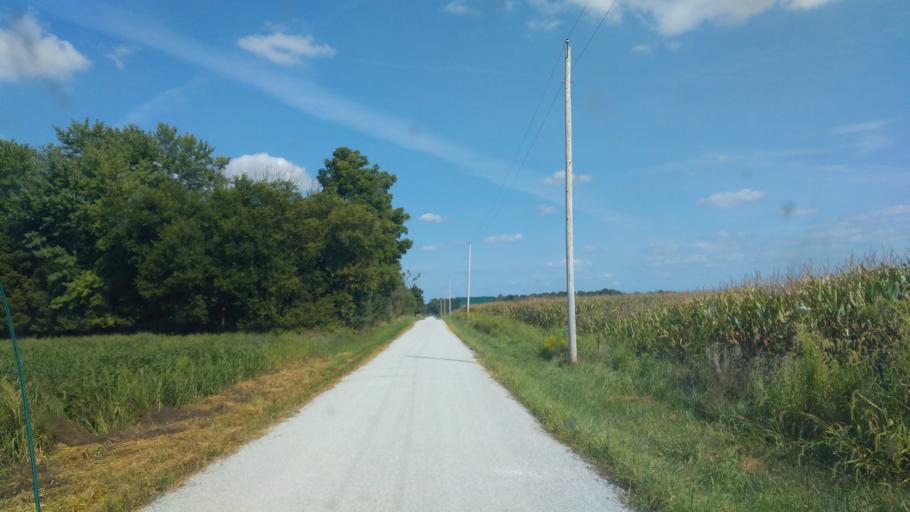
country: US
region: Ohio
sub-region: Hardin County
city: Kenton
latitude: 40.6292
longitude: -83.4549
